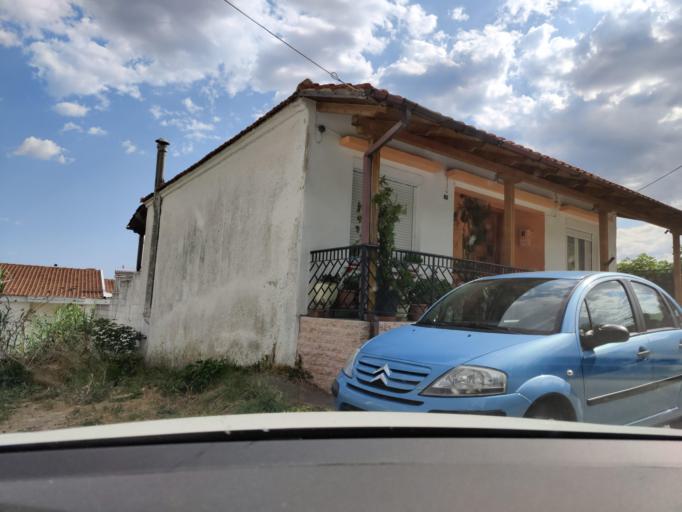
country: GR
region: Central Macedonia
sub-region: Nomos Serron
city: Serres
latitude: 41.0897
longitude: 23.5373
